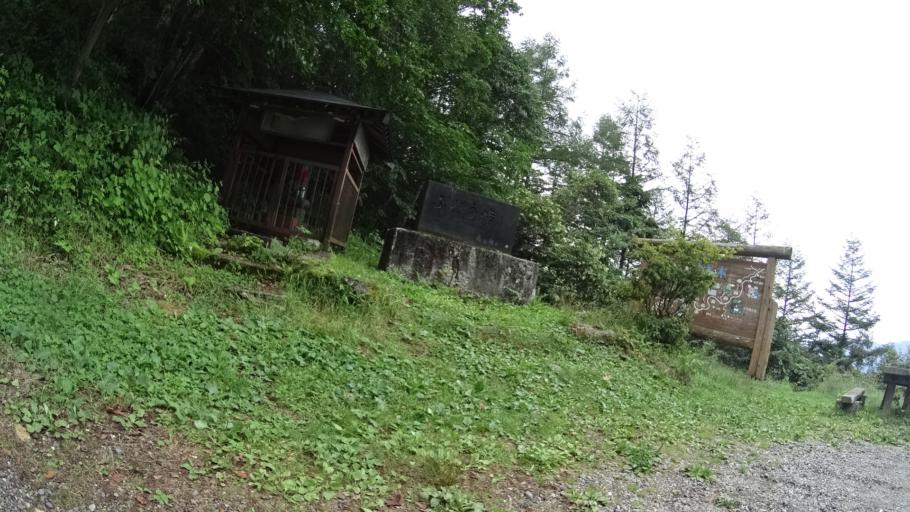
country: JP
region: Nagano
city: Saku
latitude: 36.0639
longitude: 138.6423
